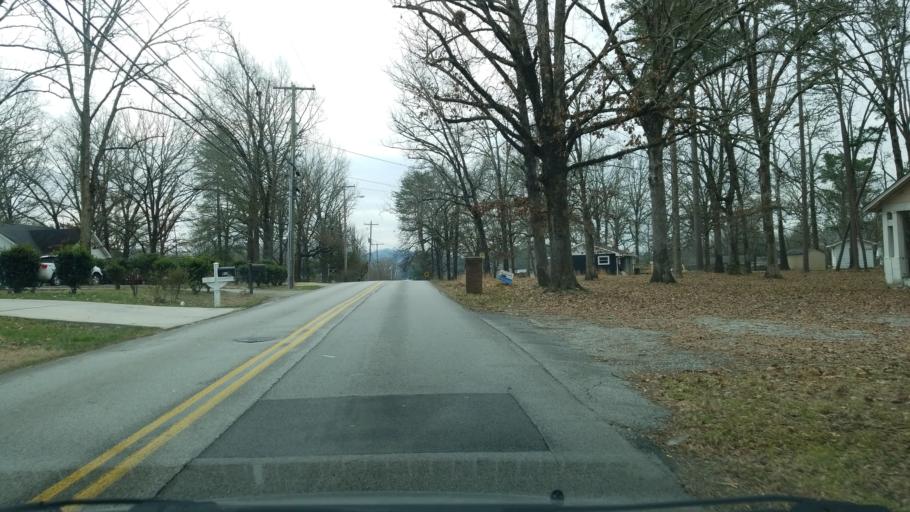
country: US
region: Tennessee
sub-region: Hamilton County
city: East Brainerd
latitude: 34.9977
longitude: -85.1487
